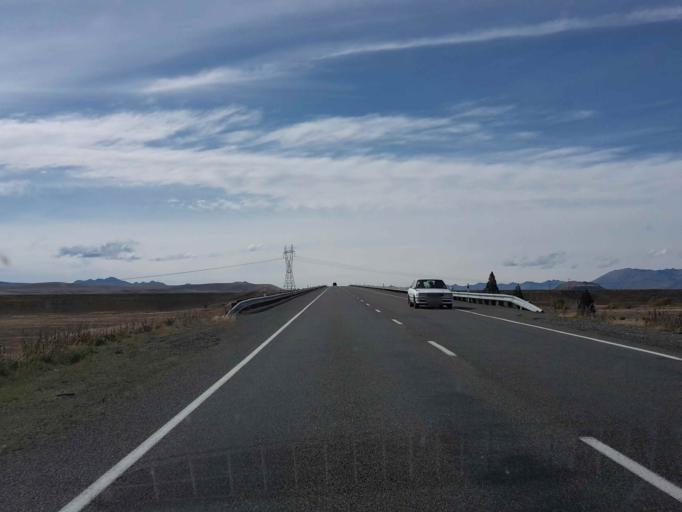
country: NZ
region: Canterbury
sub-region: Timaru District
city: Pleasant Point
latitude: -44.0764
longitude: 170.3553
